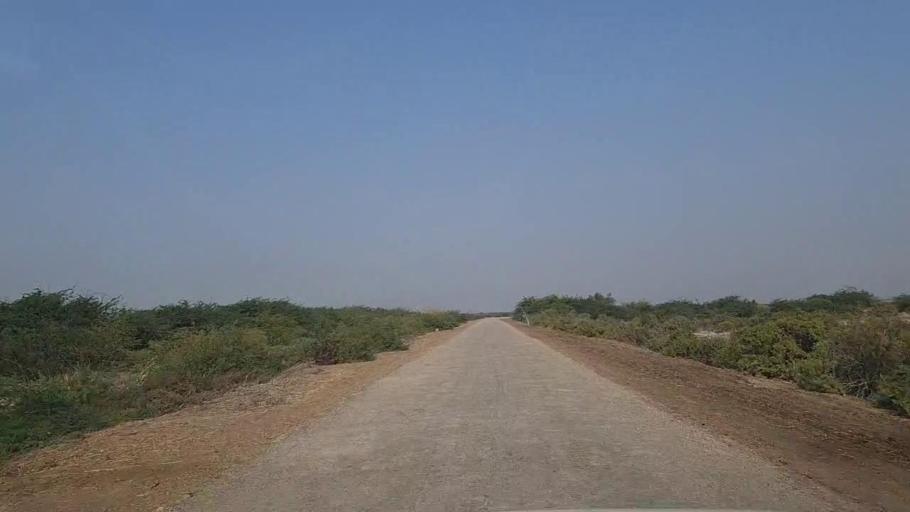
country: PK
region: Sindh
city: Keti Bandar
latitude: 24.2377
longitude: 67.6836
